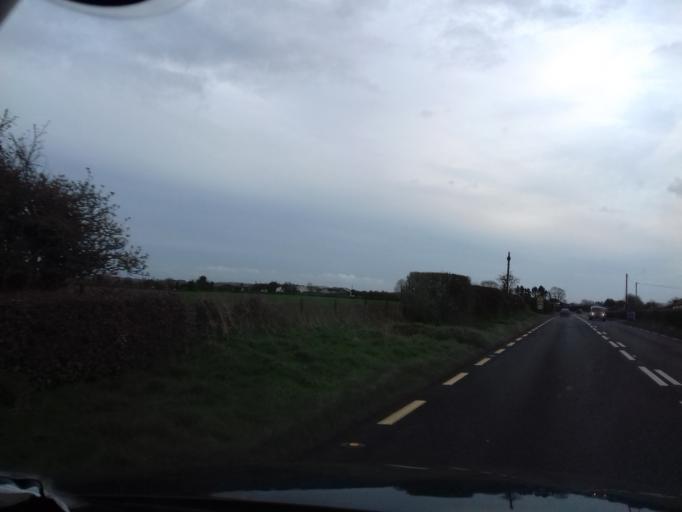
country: IE
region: Leinster
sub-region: Laois
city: Abbeyleix
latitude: 52.9272
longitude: -7.3482
